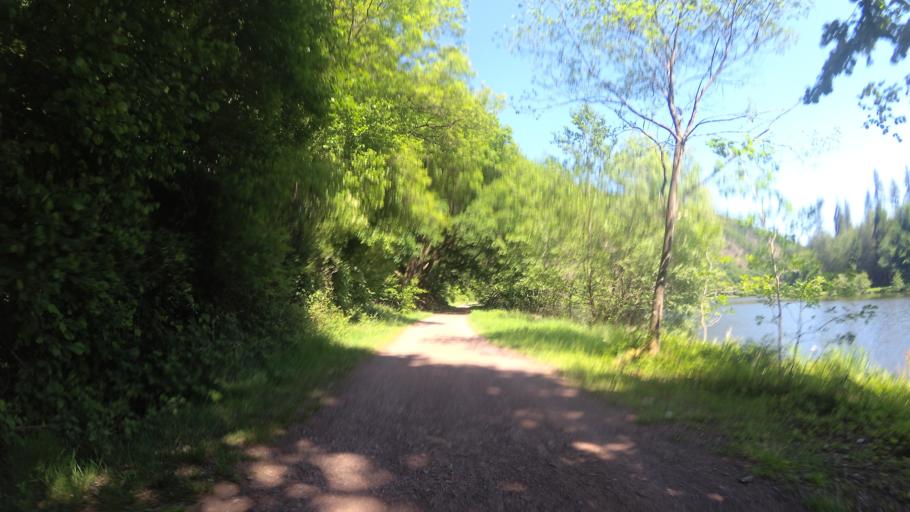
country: DE
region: Saarland
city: Orscholz
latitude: 49.5018
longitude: 6.5450
